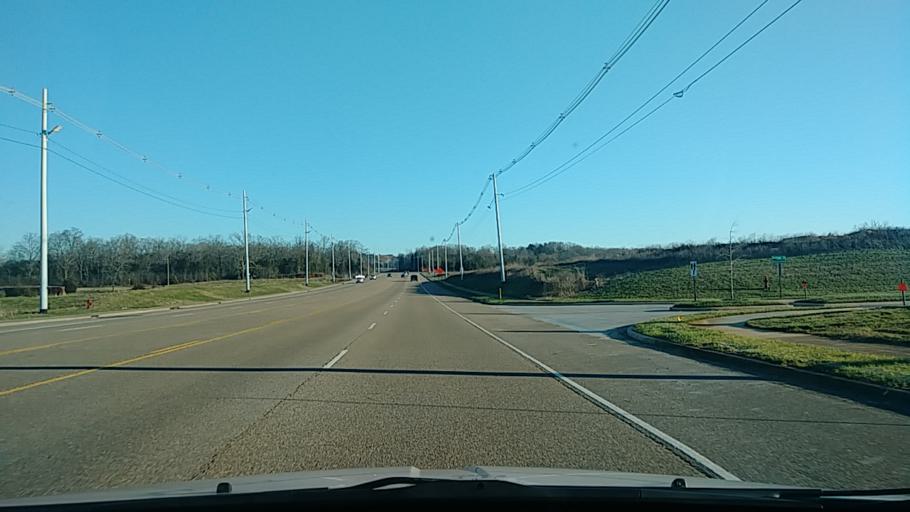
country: US
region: Tennessee
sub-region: Hamblen County
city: Morristown
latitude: 36.1856
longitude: -83.3559
